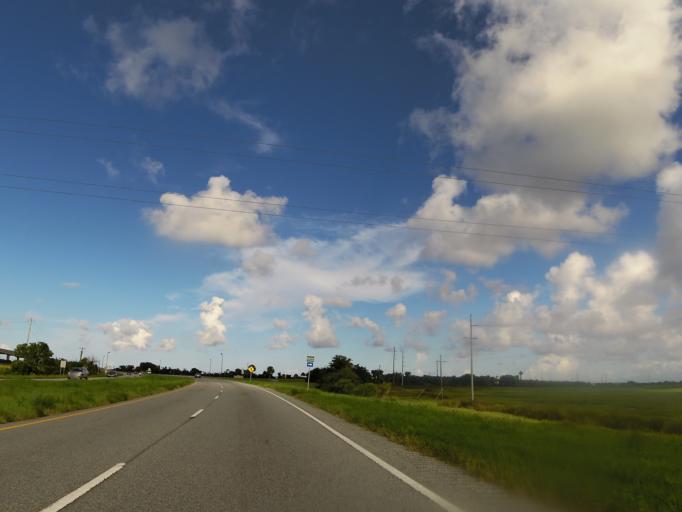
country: US
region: Georgia
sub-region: Glynn County
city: Brunswick
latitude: 31.1048
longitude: -81.4964
